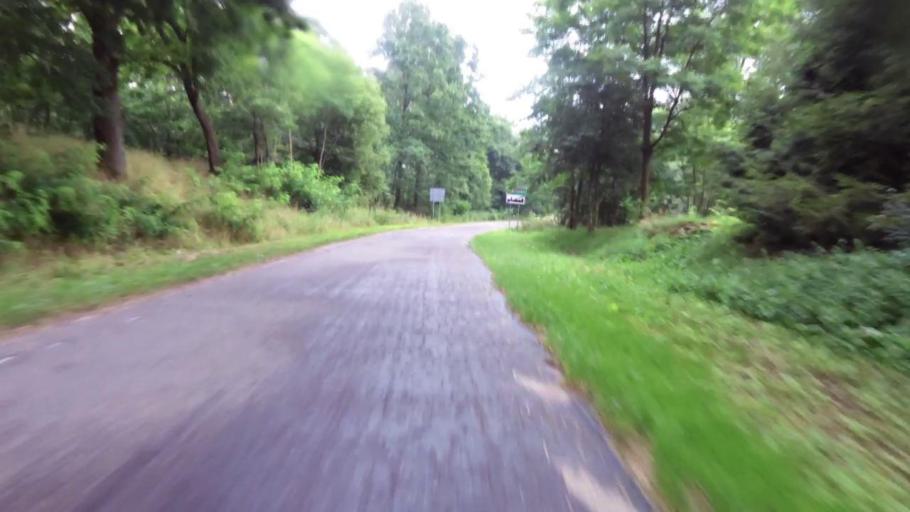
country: PL
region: West Pomeranian Voivodeship
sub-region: Powiat lobeski
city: Wegorzyno
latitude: 53.5284
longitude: 15.6483
